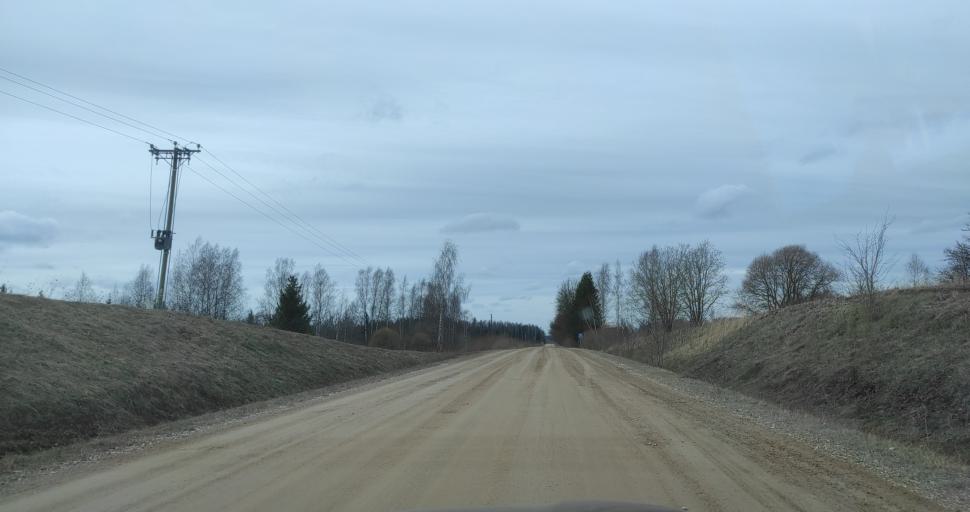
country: LV
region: Tukuma Rajons
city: Tukums
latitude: 57.0629
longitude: 23.0240
